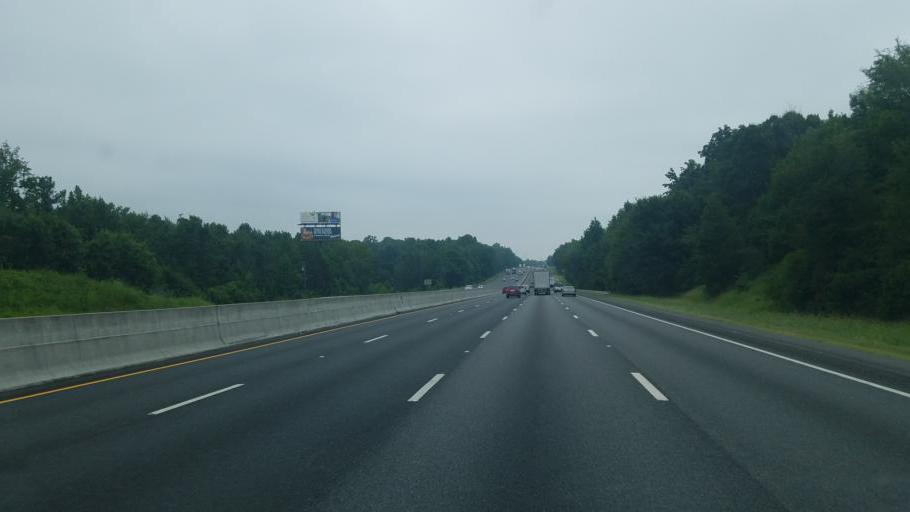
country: US
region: South Carolina
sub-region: York County
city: Fort Mill
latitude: 35.0442
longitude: -80.9594
